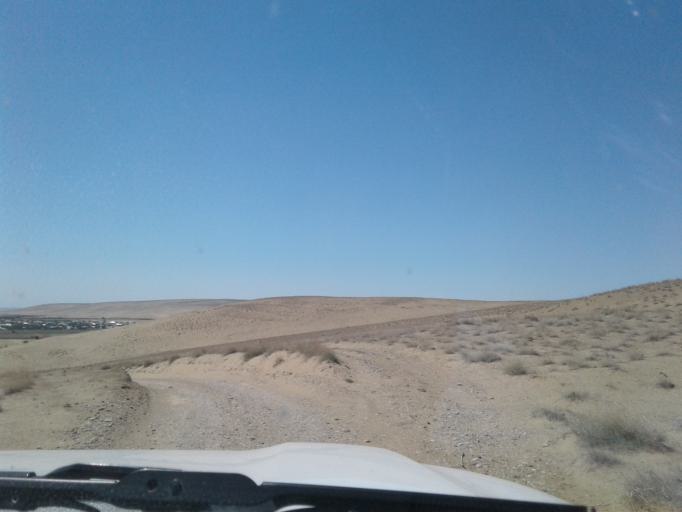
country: AF
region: Badghis
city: Bala Murghab
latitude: 35.9786
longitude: 62.9020
